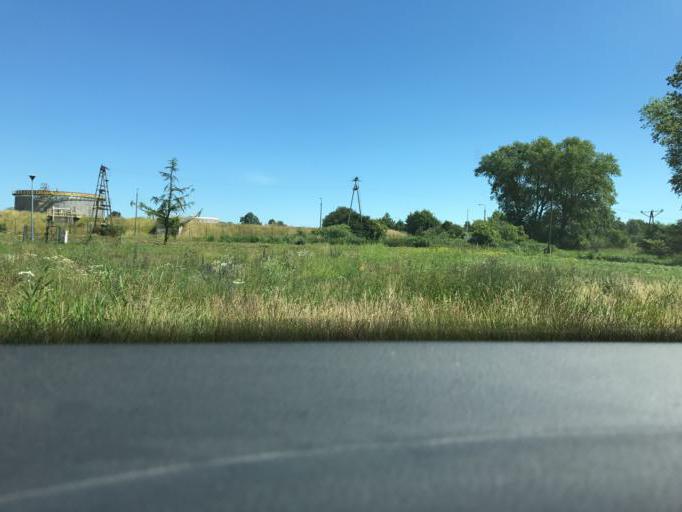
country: PL
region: Pomeranian Voivodeship
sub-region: Gdansk
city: Gdansk
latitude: 54.3380
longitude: 18.7475
